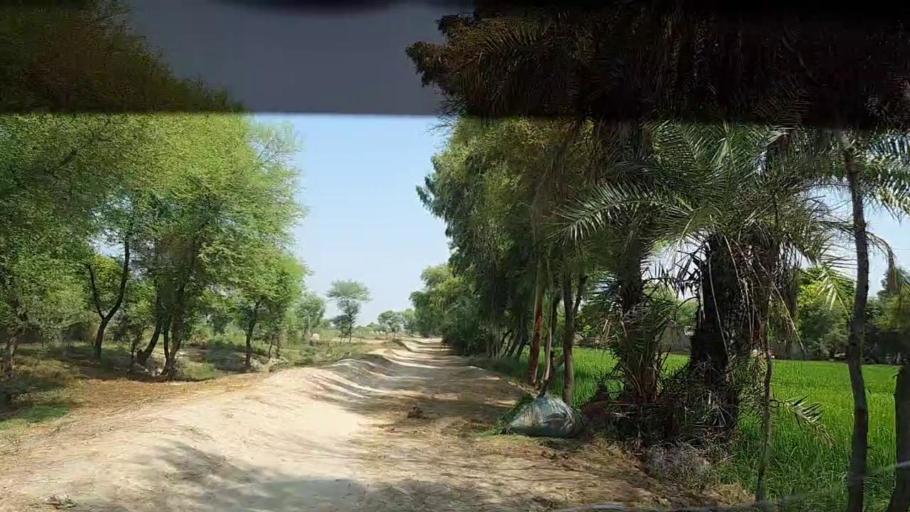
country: PK
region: Sindh
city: Tangwani
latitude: 28.2329
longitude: 68.9592
